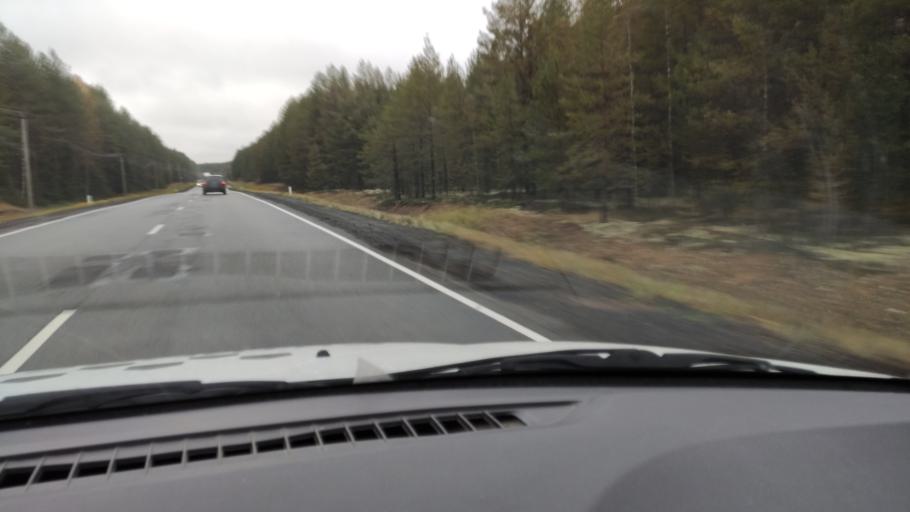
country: RU
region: Kirov
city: Belaya Kholunitsa
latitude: 58.9077
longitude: 51.0025
